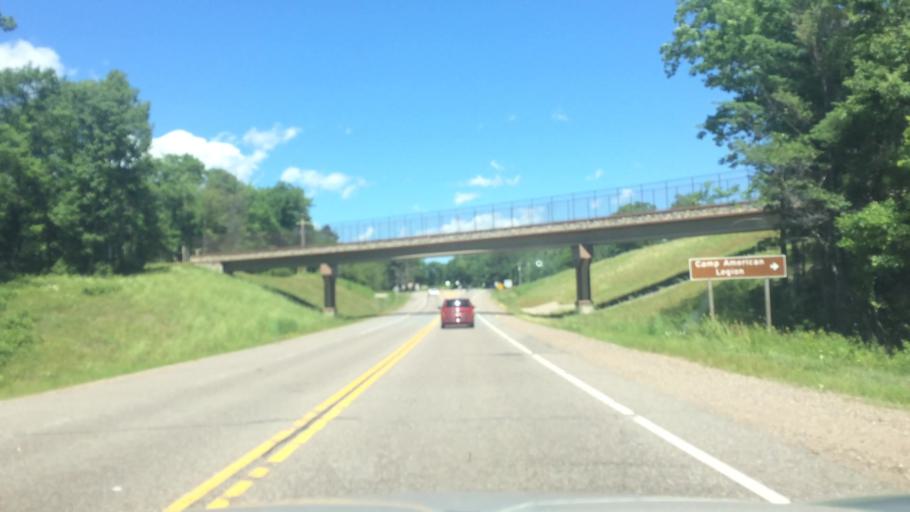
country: US
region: Wisconsin
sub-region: Vilas County
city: Lac du Flambeau
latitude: 45.7832
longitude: -89.7127
